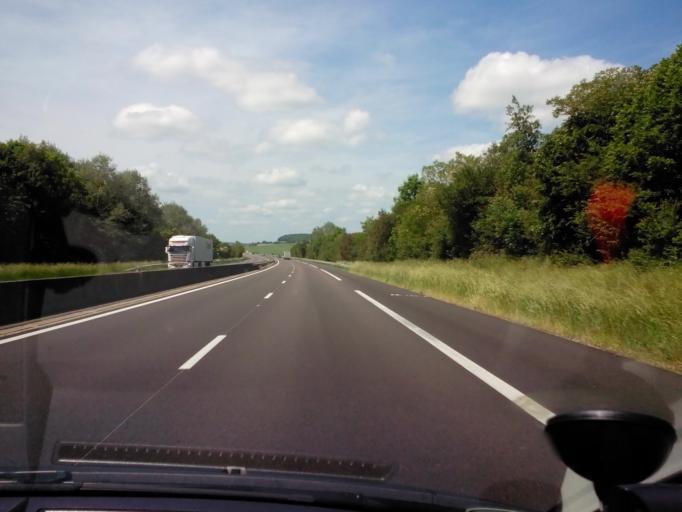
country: FR
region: Champagne-Ardenne
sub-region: Departement de la Haute-Marne
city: Nogent-le-Bas
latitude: 47.9582
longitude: 5.3902
